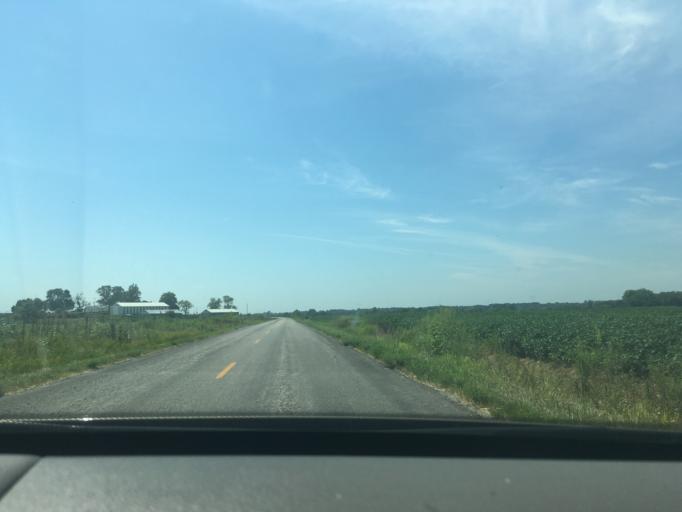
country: US
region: Missouri
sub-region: Nodaway County
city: Maryville
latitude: 40.2020
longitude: -94.7378
